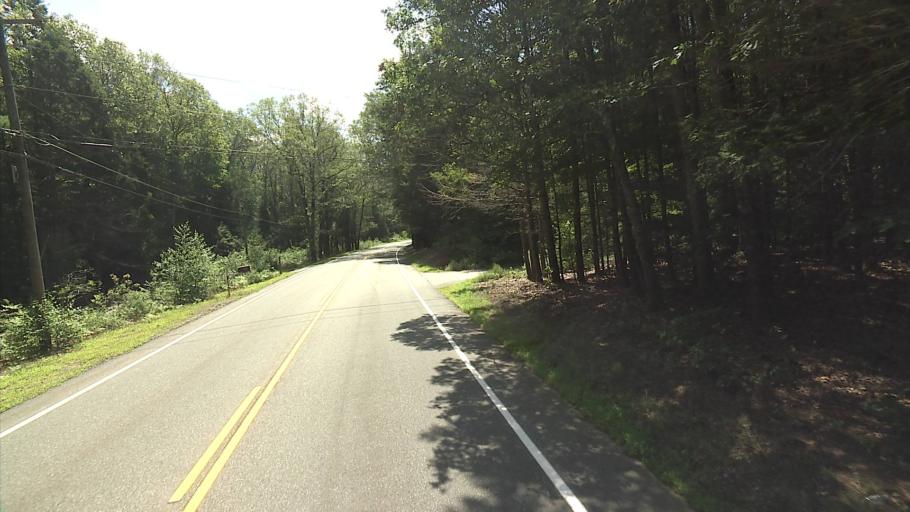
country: US
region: Massachusetts
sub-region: Worcester County
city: Southbridge
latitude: 41.9640
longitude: -72.0795
